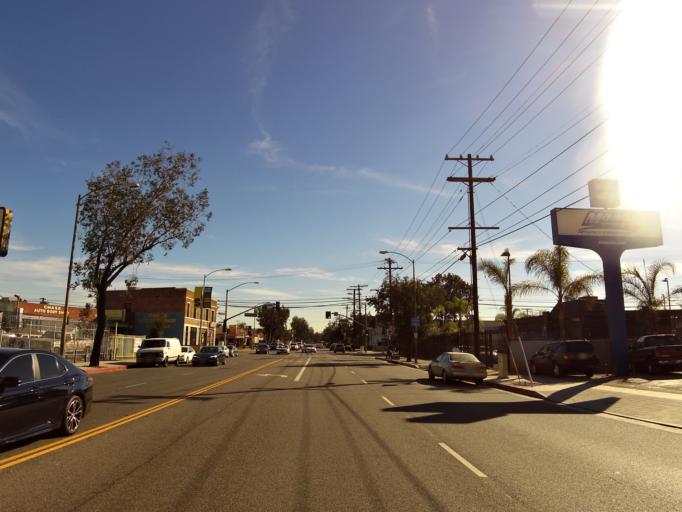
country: US
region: California
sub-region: Los Angeles County
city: Glendale
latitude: 34.1342
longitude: -118.2629
